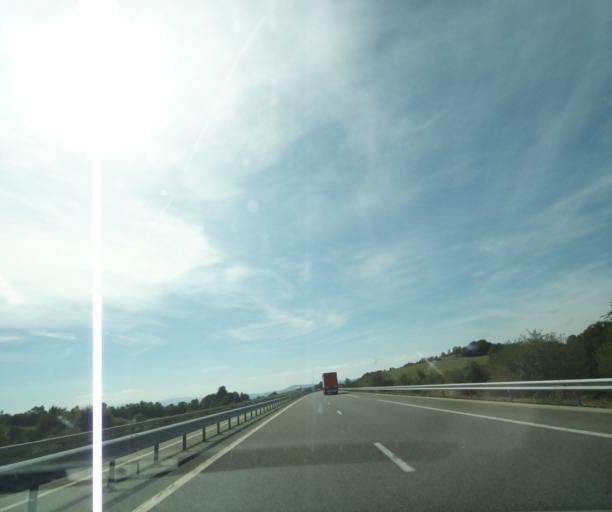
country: FR
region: Auvergne
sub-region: Departement du Puy-de-Dome
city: Saint-Ours
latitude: 45.8747
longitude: 2.9055
